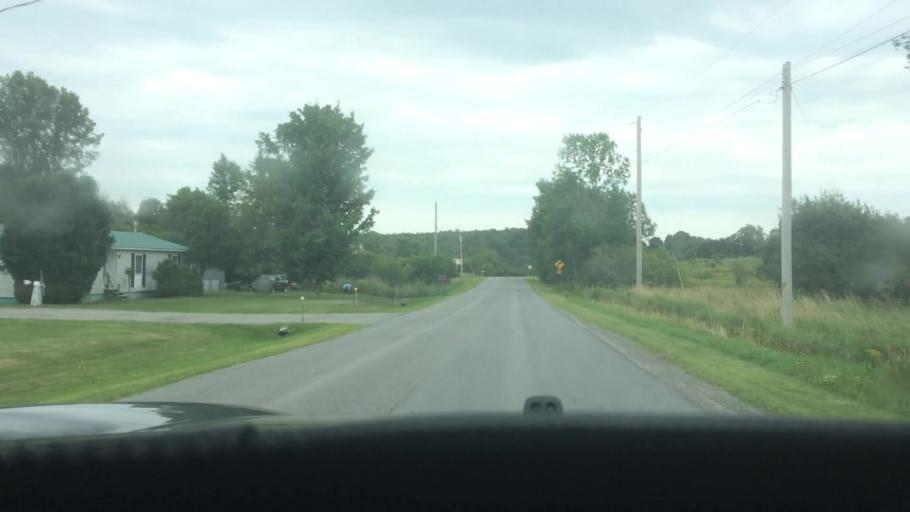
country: US
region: New York
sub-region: St. Lawrence County
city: Canton
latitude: 44.5541
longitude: -75.1350
